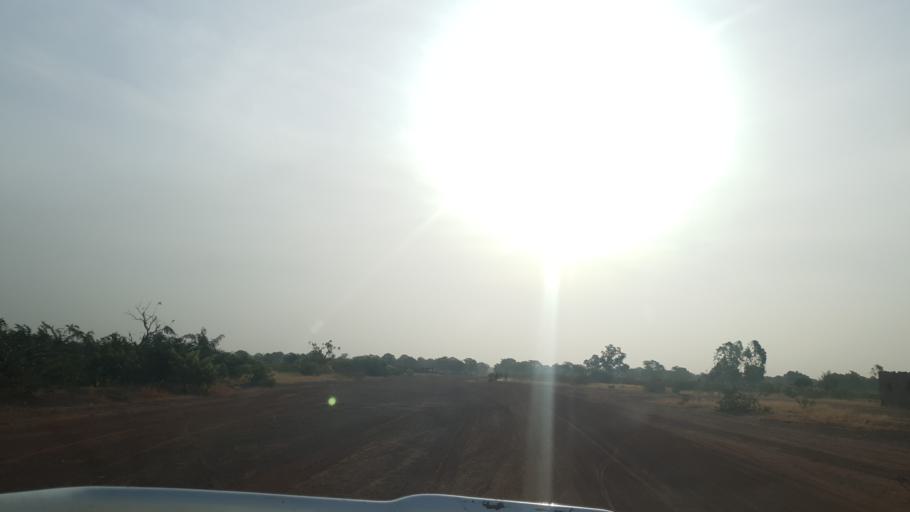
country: ML
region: Koulikoro
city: Dioila
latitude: 12.7645
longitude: -6.9142
